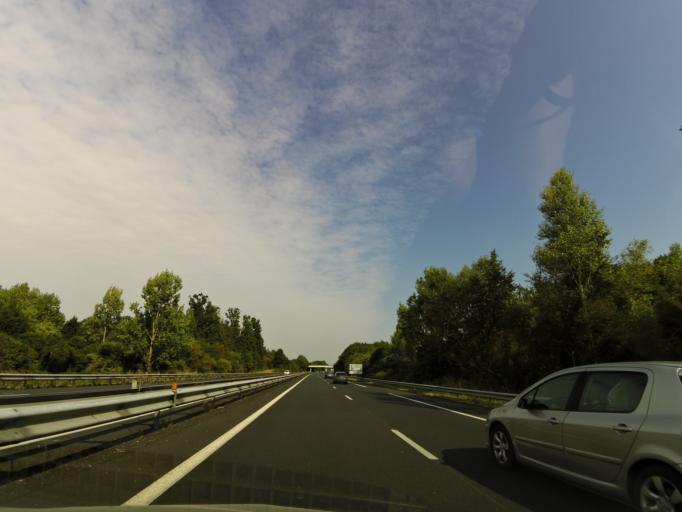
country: FR
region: Pays de la Loire
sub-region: Departement de la Vendee
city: Bouffere
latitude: 46.9413
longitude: -1.3485
